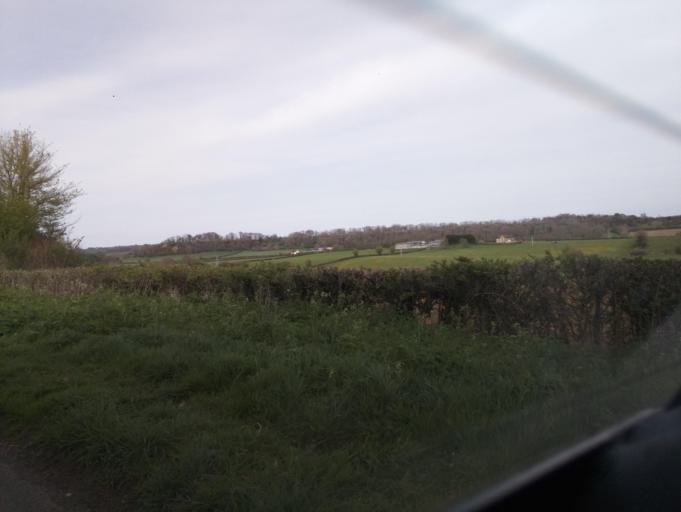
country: GB
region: England
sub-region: Somerset
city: Milborne Port
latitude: 50.9742
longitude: -2.4690
